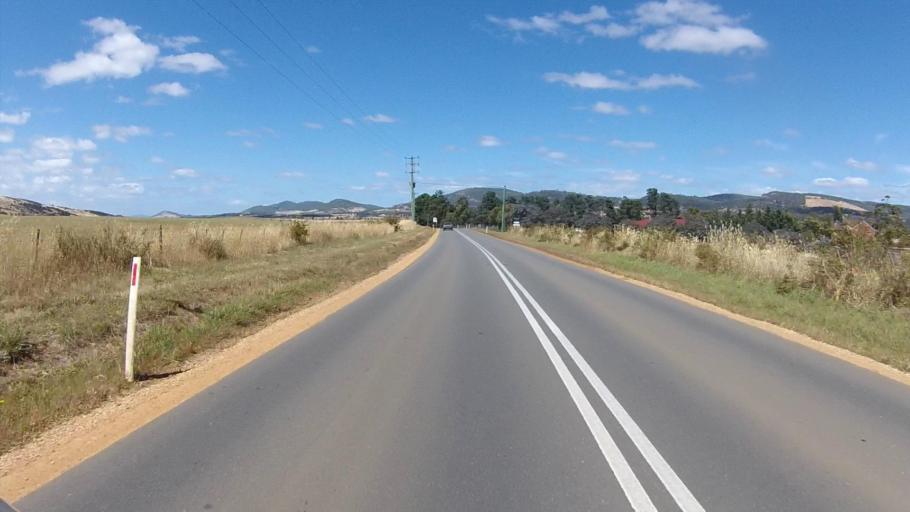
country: AU
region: Tasmania
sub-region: Clarence
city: Cambridge
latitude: -42.7508
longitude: 147.4165
